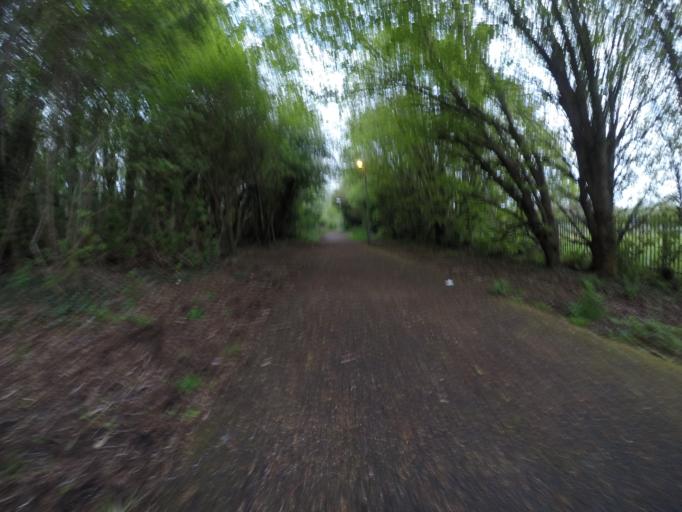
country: GB
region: Scotland
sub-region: North Ayrshire
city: Irvine
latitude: 55.6334
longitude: -4.6298
